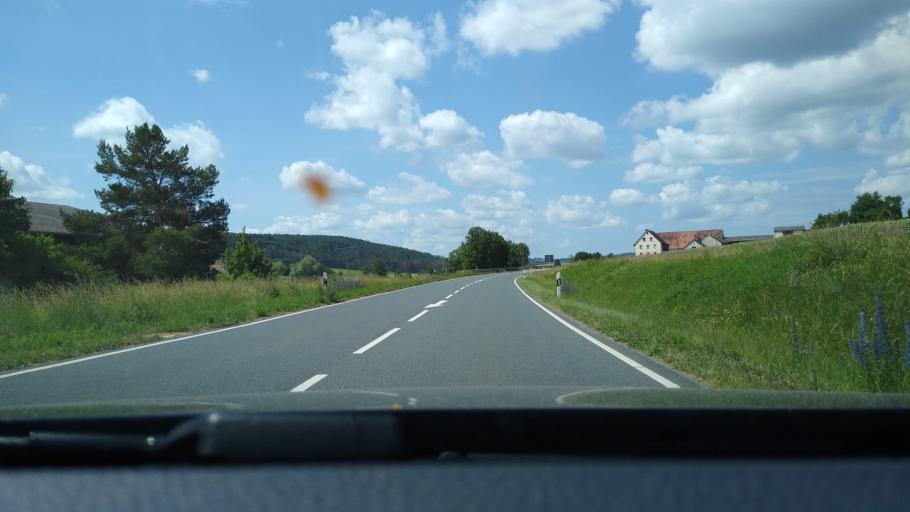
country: DE
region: Bavaria
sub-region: Regierungsbezirk Mittelfranken
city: Neuhof an der Zenn
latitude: 49.4595
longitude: 10.6408
